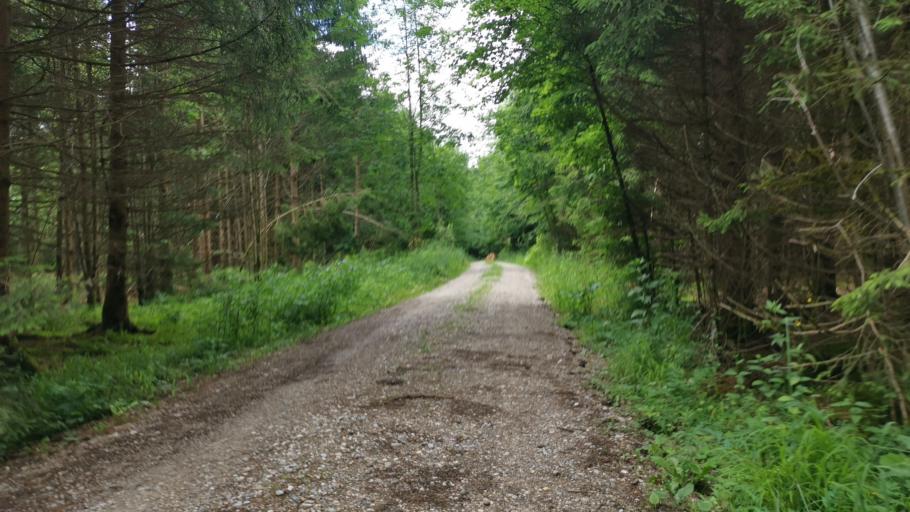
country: DE
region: Bavaria
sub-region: Upper Bavaria
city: Schaftlarn
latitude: 48.0090
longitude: 11.4649
